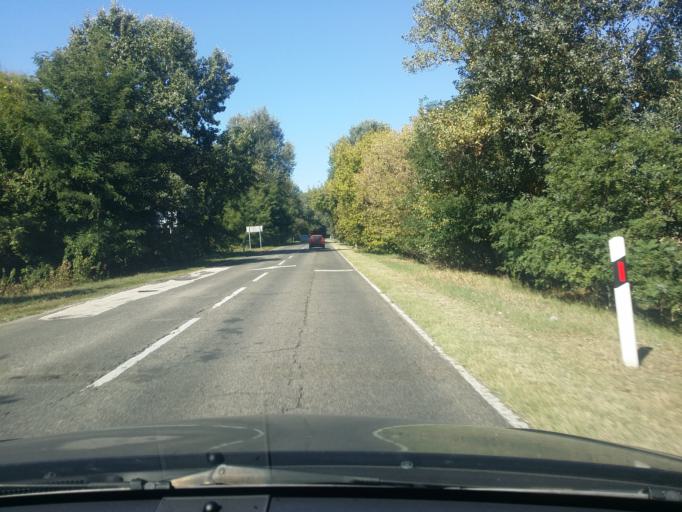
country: HU
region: Csongrad
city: Pusztaszer
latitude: 46.5338
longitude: 19.9616
